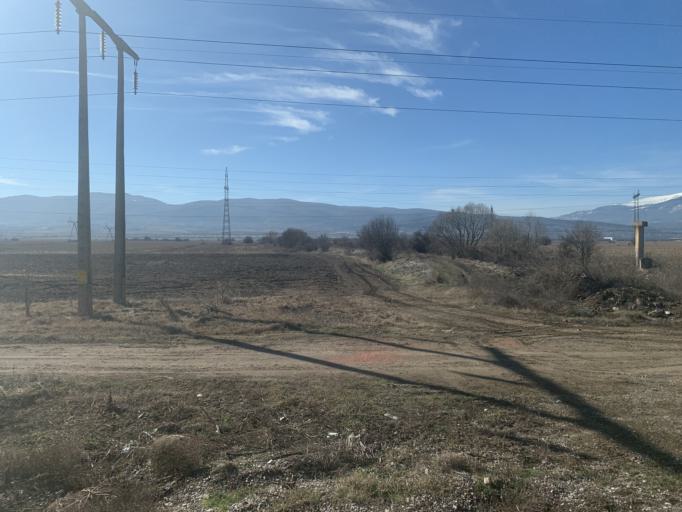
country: BG
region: Sofiya
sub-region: Obshtina Elin Pelin
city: Elin Pelin
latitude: 42.6500
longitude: 23.4802
